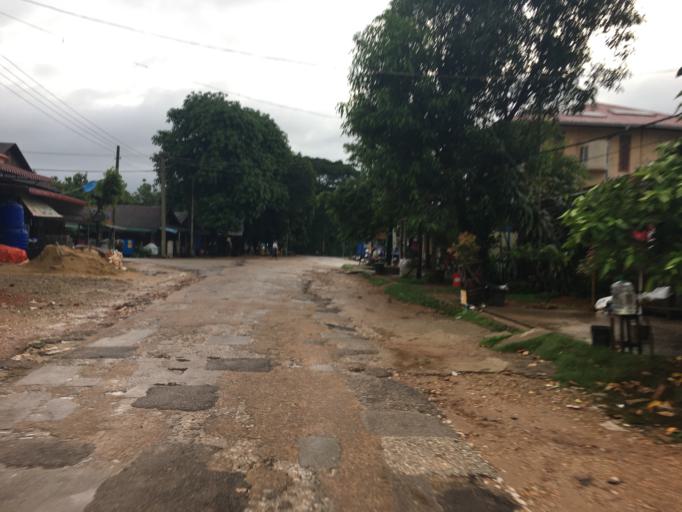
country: MM
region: Mon
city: Mudon
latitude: 16.0411
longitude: 98.1206
